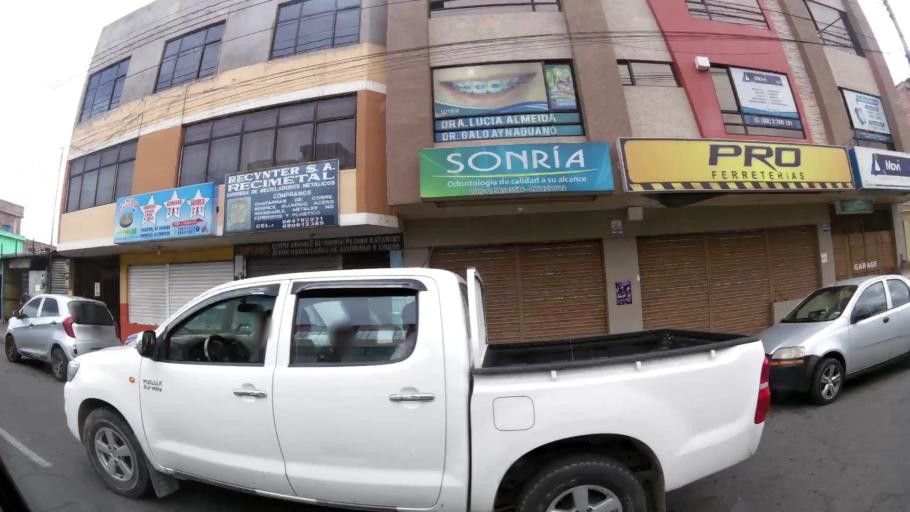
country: EC
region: Tungurahua
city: Ambato
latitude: -1.2760
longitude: -78.6300
